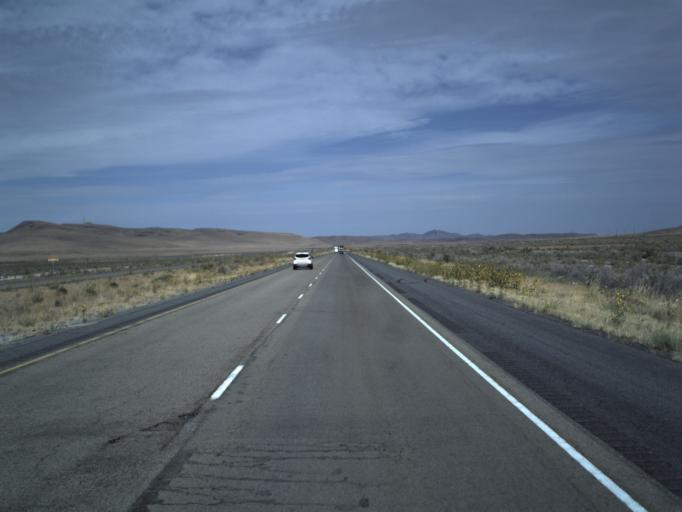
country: US
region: Utah
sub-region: Tooele County
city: Grantsville
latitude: 40.7771
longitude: -112.8072
